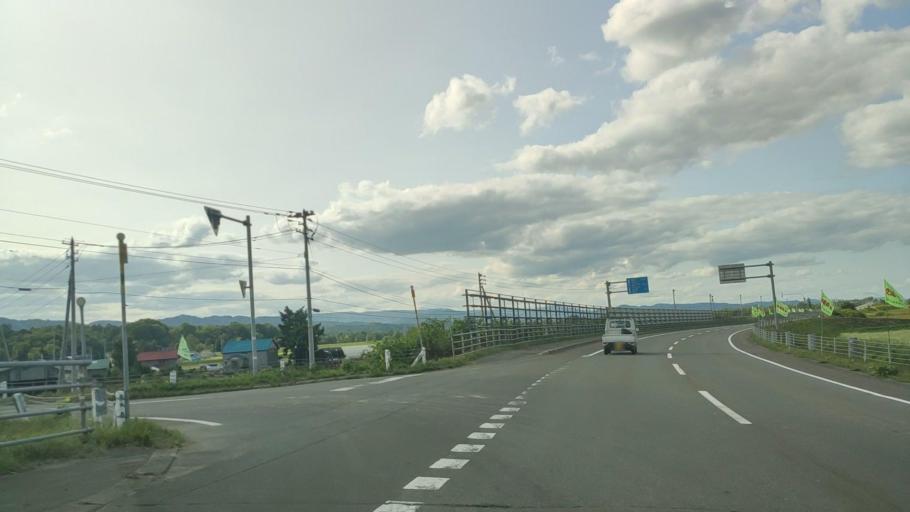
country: JP
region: Hokkaido
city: Nayoro
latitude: 44.4465
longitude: 142.3636
